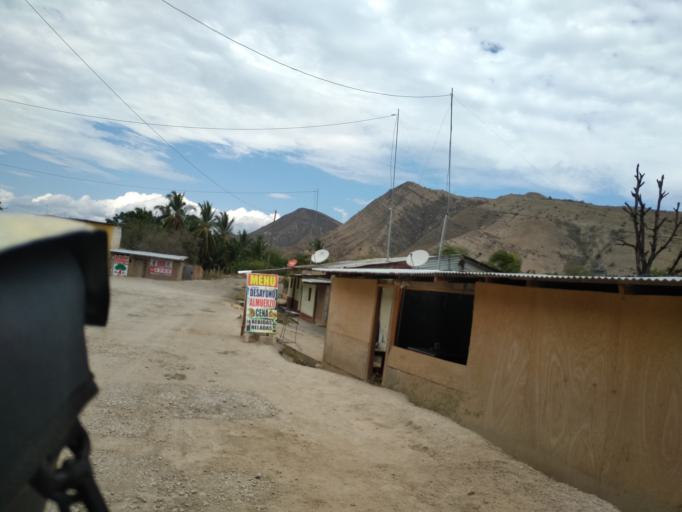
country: PE
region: Cajamarca
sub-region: Provincia de Jaen
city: Bellavista
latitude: -5.7538
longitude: -78.6903
